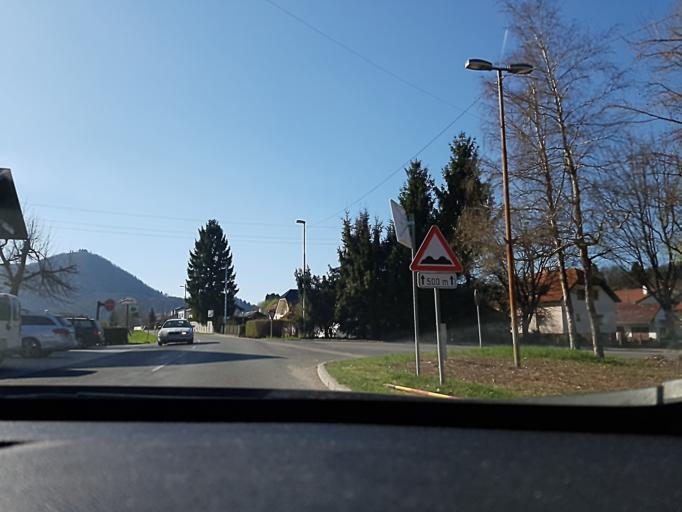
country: SI
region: Vodice
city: Vodice
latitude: 46.1265
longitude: 14.4974
